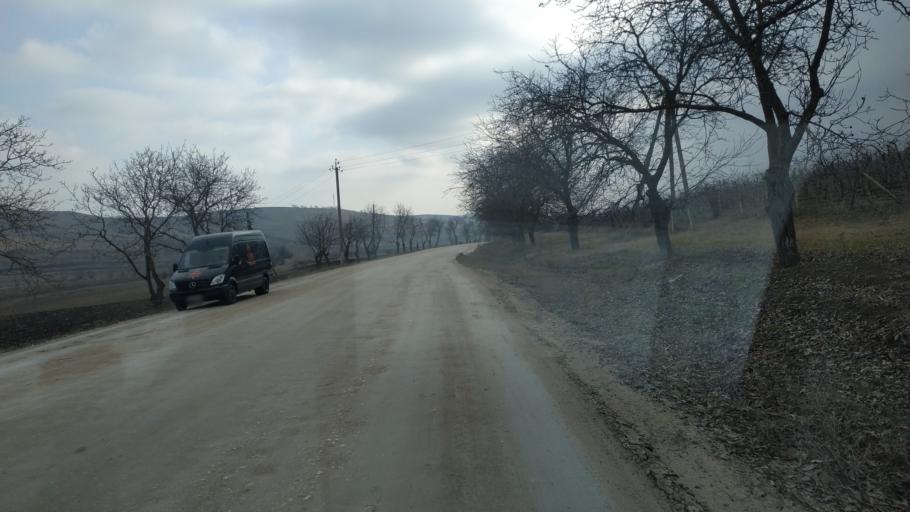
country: MD
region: Hincesti
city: Dancu
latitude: 46.9177
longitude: 28.3291
